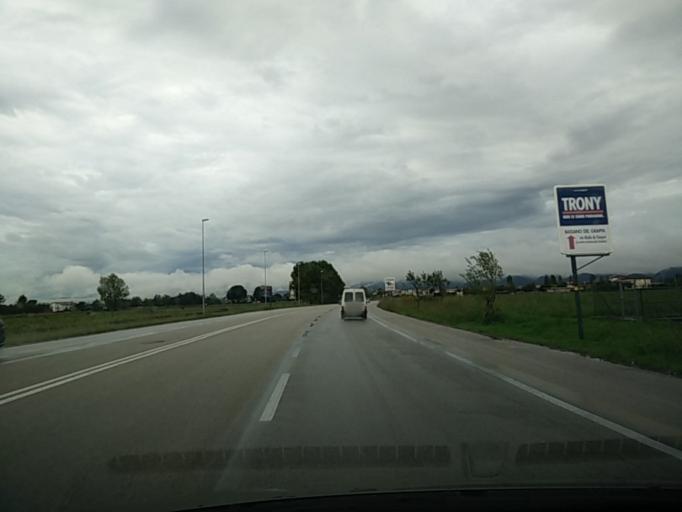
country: IT
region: Veneto
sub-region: Provincia di Vicenza
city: San Zeno-San Giuseppe
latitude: 45.7431
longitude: 11.7466
